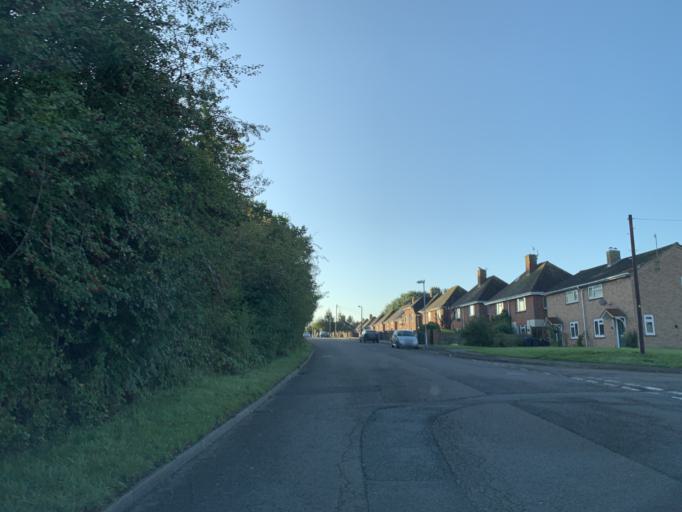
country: GB
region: England
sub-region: Wiltshire
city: Salisbury
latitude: 51.0848
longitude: -1.8046
